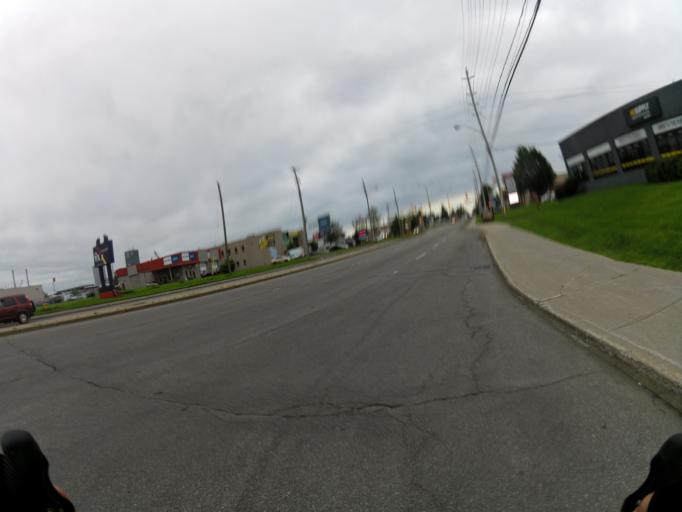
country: CA
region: Ontario
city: Ottawa
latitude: 45.3310
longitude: -75.7219
